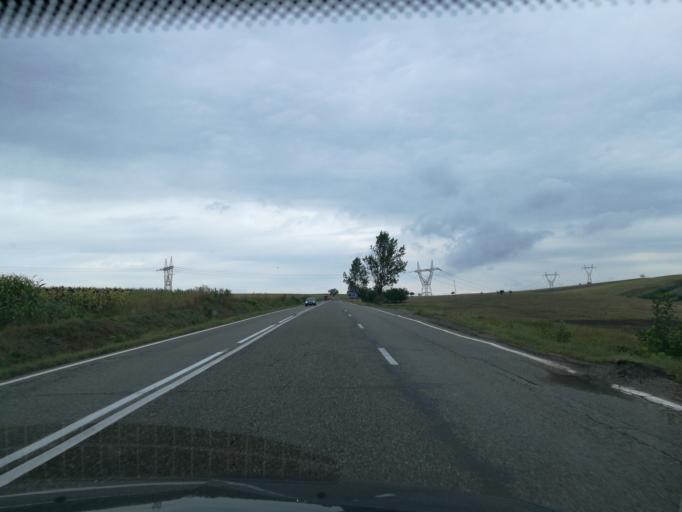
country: RO
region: Suceava
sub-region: Comuna Bunesti
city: Bunesti
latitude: 47.5367
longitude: 26.2718
